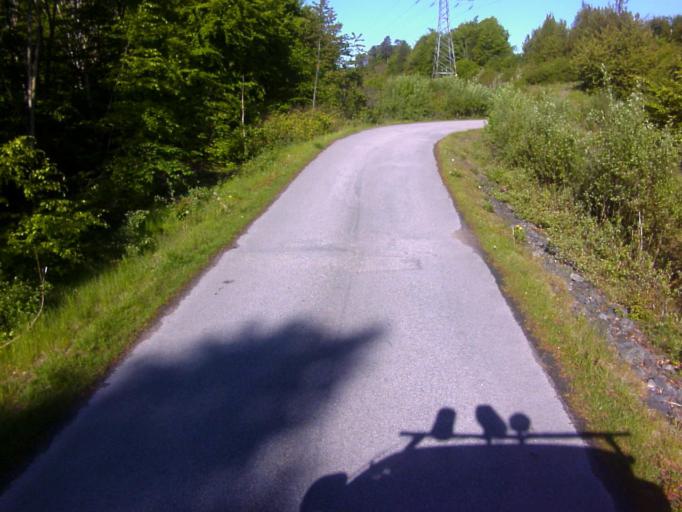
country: SE
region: Blekinge
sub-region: Solvesborgs Kommun
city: Soelvesborg
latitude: 56.0647
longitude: 14.5925
